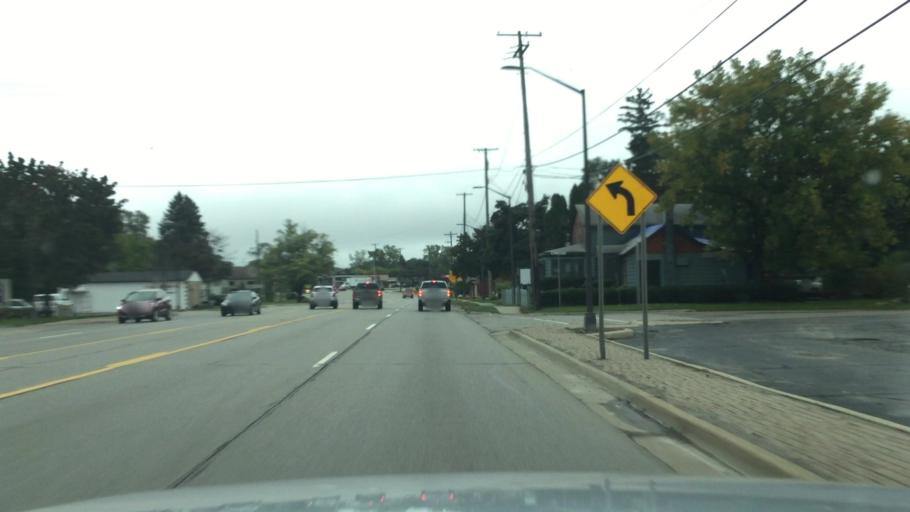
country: US
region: Michigan
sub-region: Oakland County
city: Waterford
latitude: 42.7049
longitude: -83.4046
